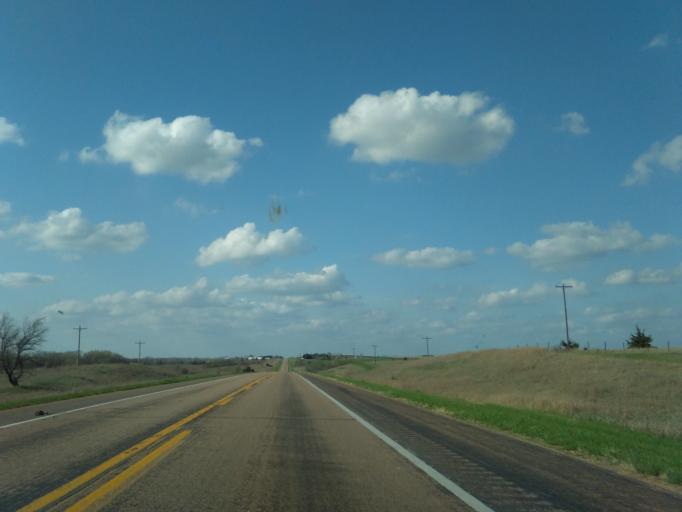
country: US
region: Nebraska
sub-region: Webster County
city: Red Cloud
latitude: 40.1271
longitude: -98.5189
